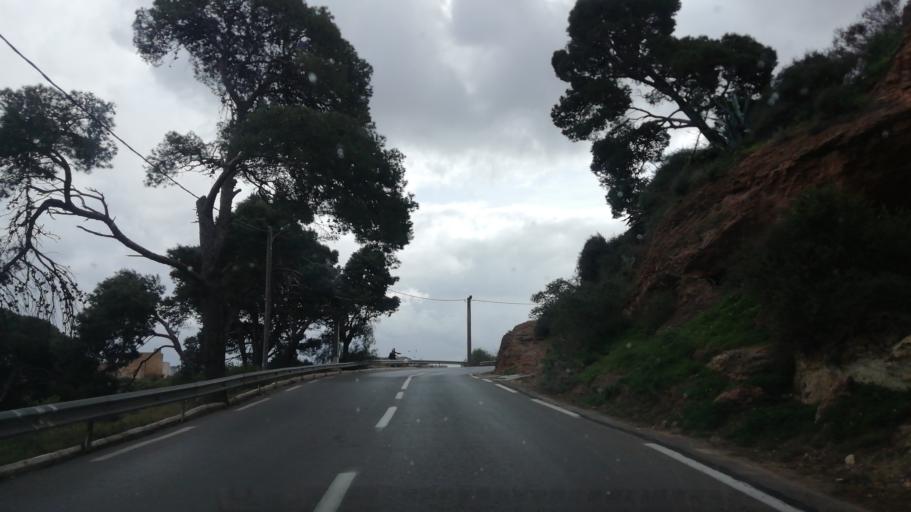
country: DZ
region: Oran
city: Oran
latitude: 35.7042
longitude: -0.6607
